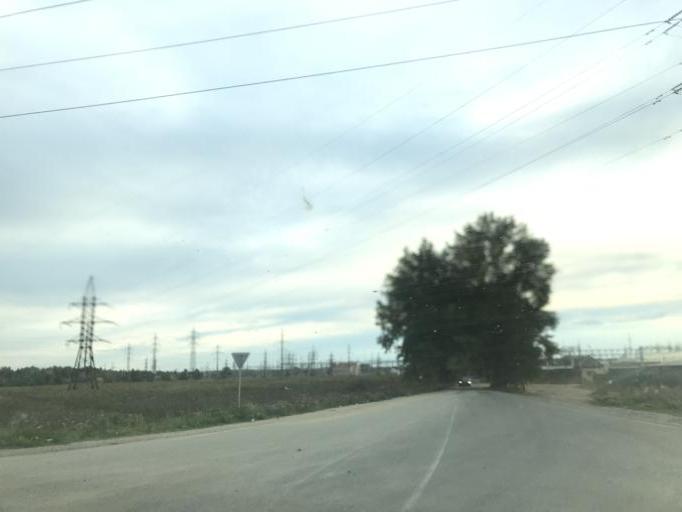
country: RU
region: Chelyabinsk
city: Roshchino
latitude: 55.2329
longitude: 61.2821
